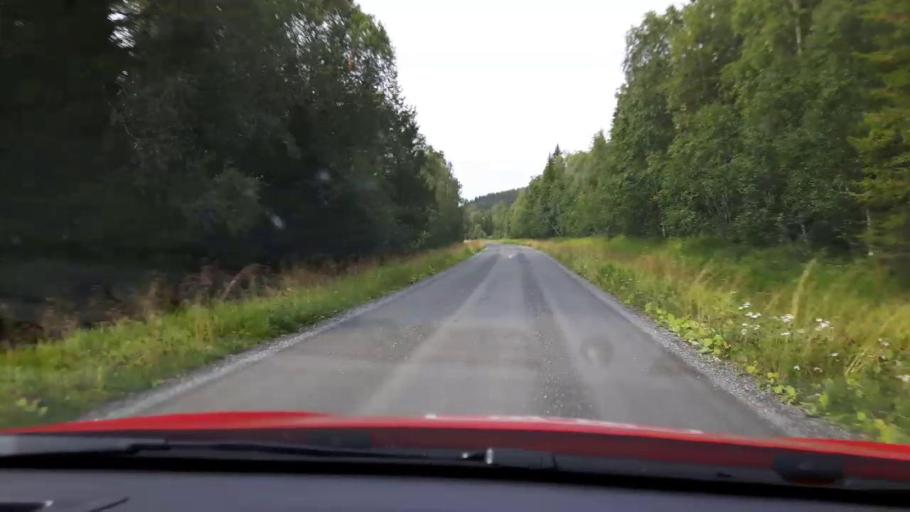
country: SE
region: Jaemtland
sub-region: Are Kommun
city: Are
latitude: 63.7407
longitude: 13.0059
